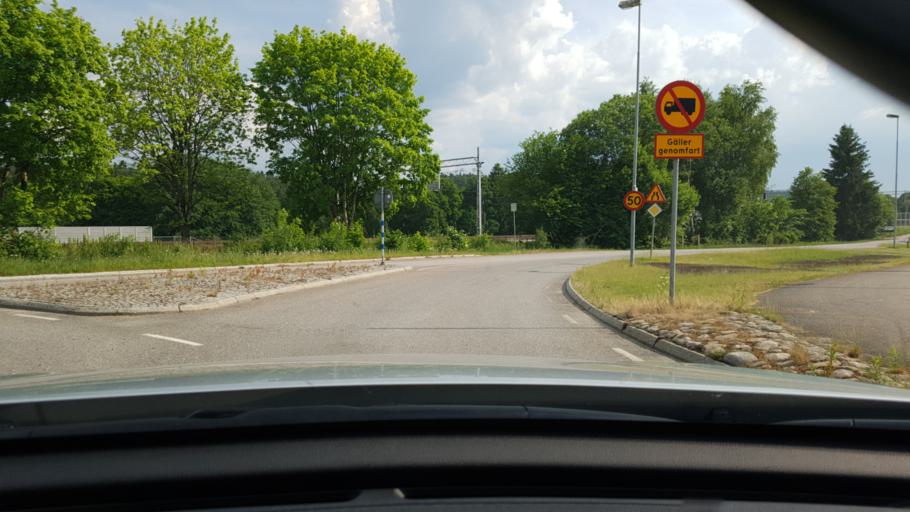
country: SE
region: Vaestra Goetaland
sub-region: Lerums Kommun
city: Stenkullen
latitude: 57.7952
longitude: 12.3177
